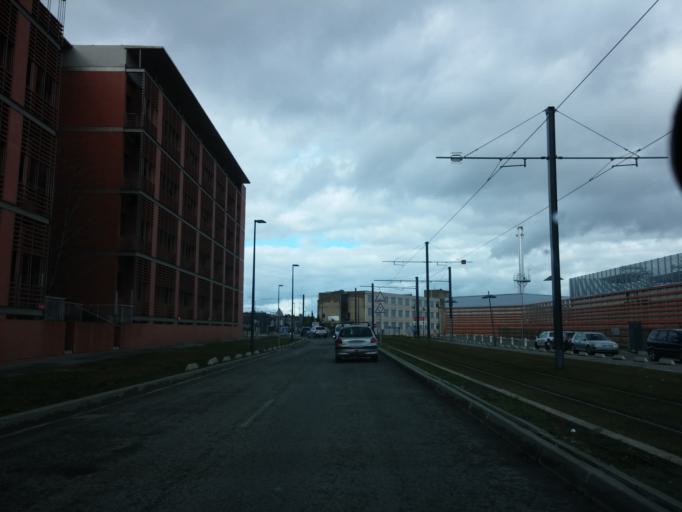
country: FR
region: Midi-Pyrenees
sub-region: Departement de la Haute-Garonne
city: Blagnac
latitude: 43.6106
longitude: 1.4018
